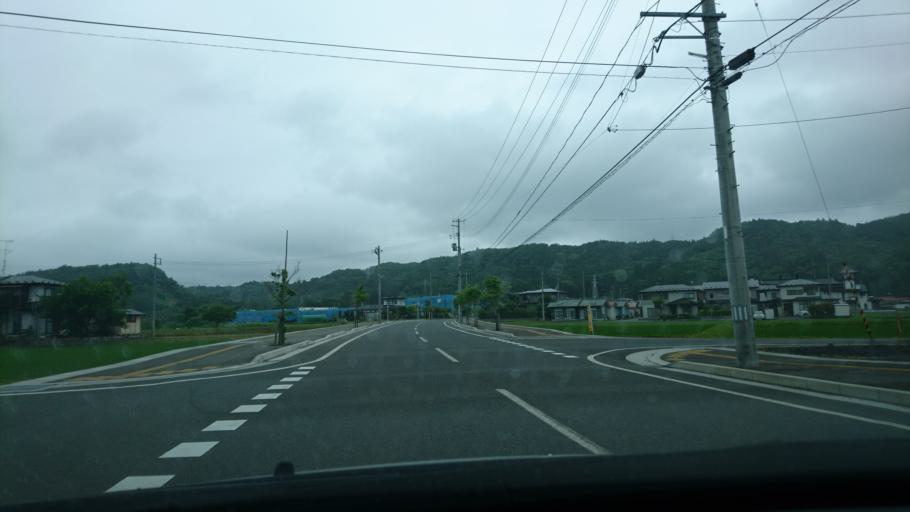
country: JP
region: Iwate
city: Ichinoseki
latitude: 38.9383
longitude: 141.0834
